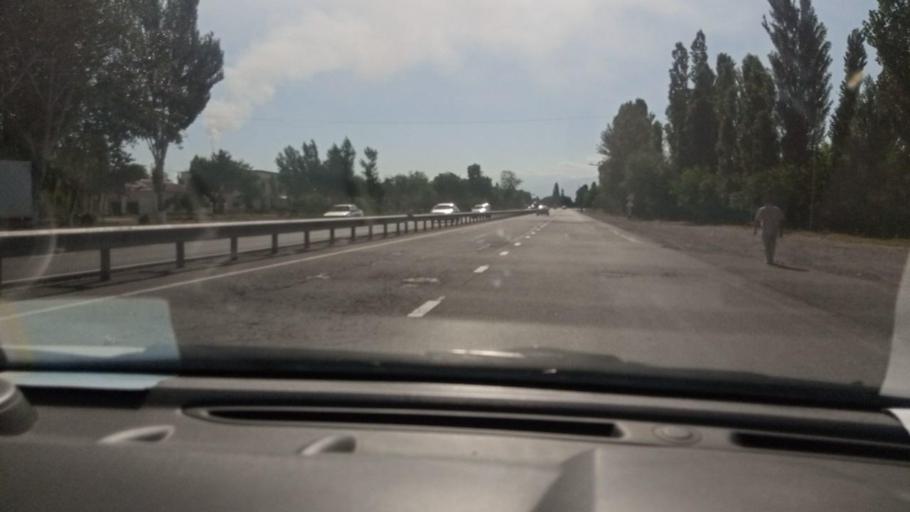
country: UZ
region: Toshkent
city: Ohangaron
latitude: 40.9085
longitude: 69.7643
